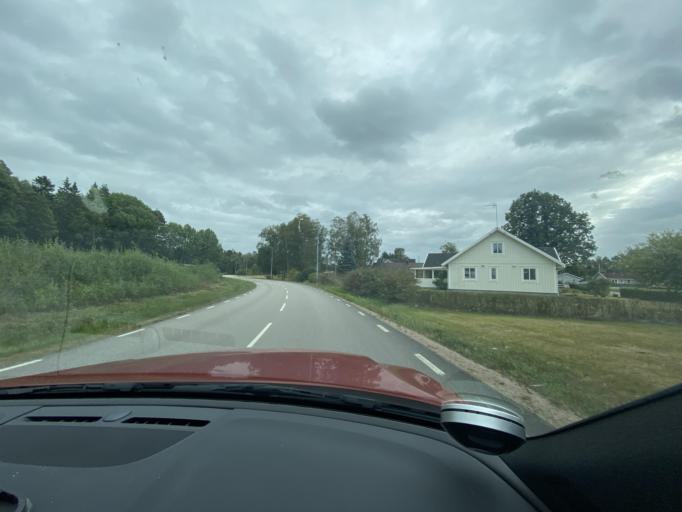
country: SE
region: Kronoberg
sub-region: Markaryds Kommun
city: Markaryd
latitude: 56.4867
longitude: 13.5289
